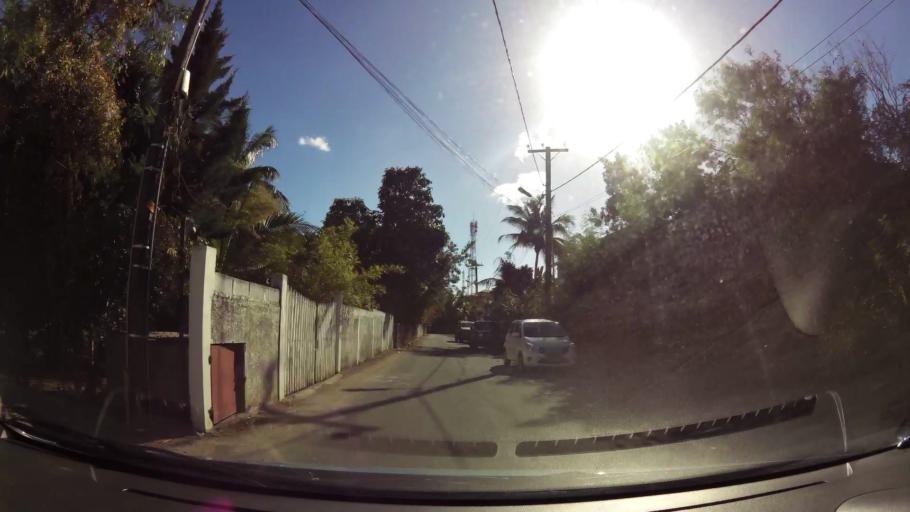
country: MU
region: Black River
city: Grande Riviere Noire
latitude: -20.3530
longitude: 57.3627
